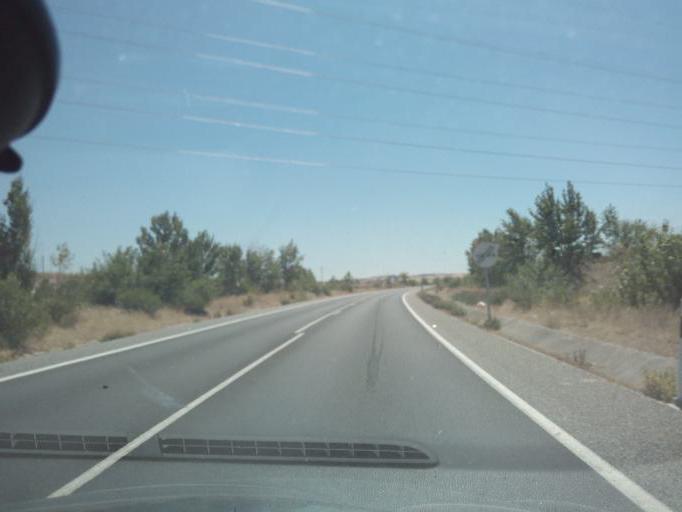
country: ES
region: Madrid
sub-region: Provincia de Madrid
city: Cobena
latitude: 40.5831
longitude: -3.5489
